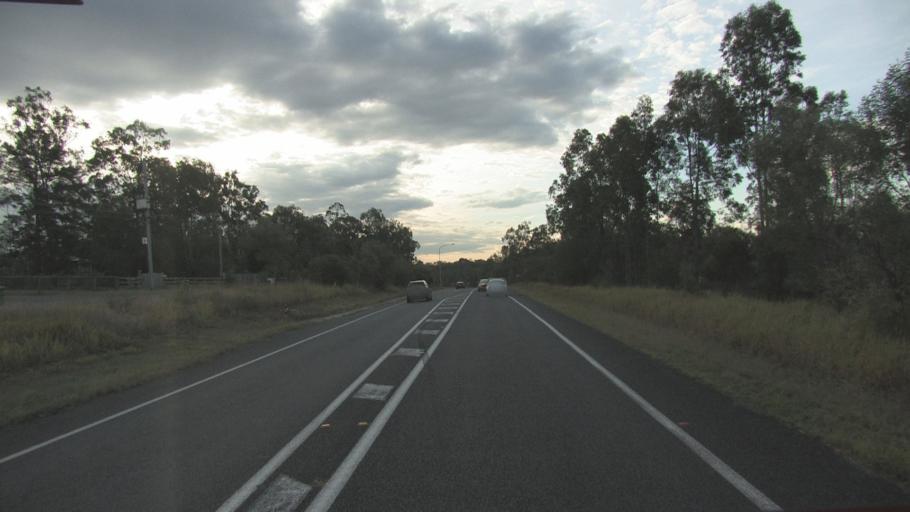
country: AU
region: Queensland
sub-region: Logan
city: Cedar Vale
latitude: -27.8458
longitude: 153.1195
